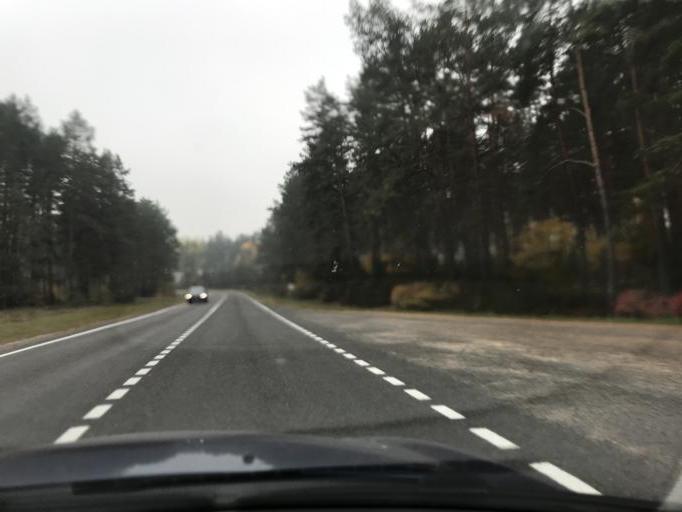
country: BY
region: Grodnenskaya
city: Hrodna
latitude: 53.8496
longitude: 23.8907
